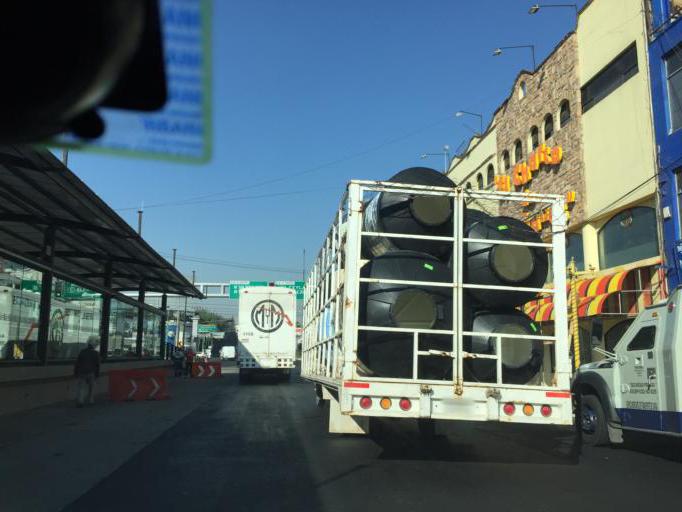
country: MX
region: Mexico
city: Colonia Lindavista
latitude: 19.4933
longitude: -99.1453
